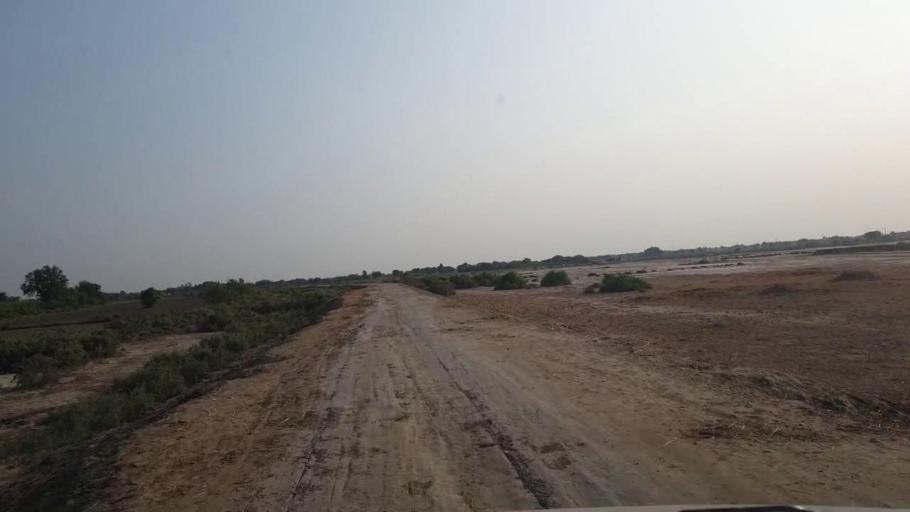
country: PK
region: Sindh
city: Rajo Khanani
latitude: 25.0454
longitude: 68.7664
